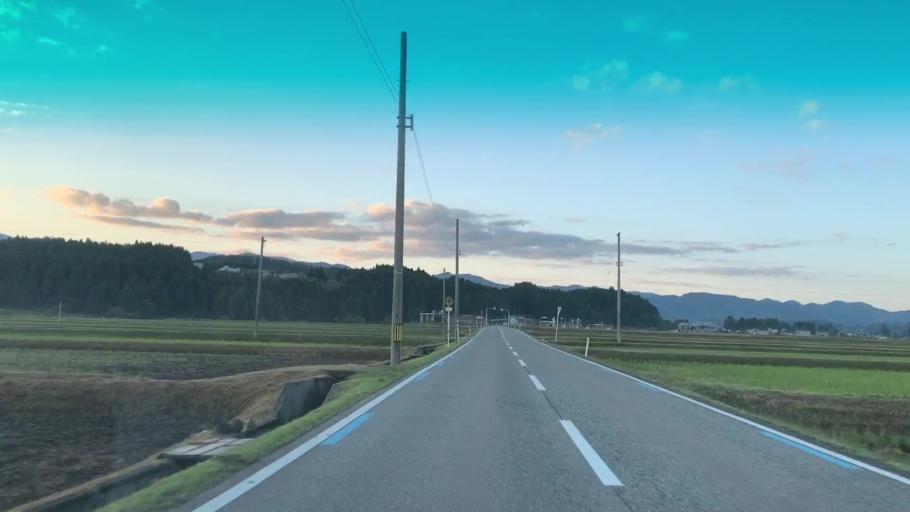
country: JP
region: Toyama
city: Kamiichi
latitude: 36.6242
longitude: 137.3286
